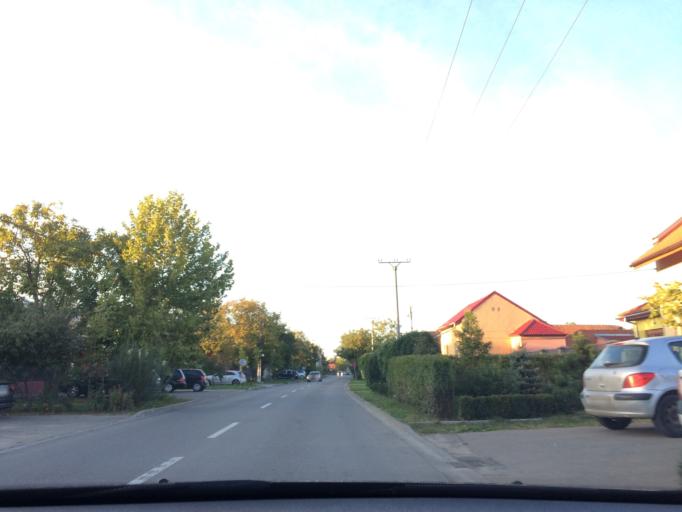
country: RO
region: Timis
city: Timisoara
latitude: 45.7610
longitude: 21.1954
